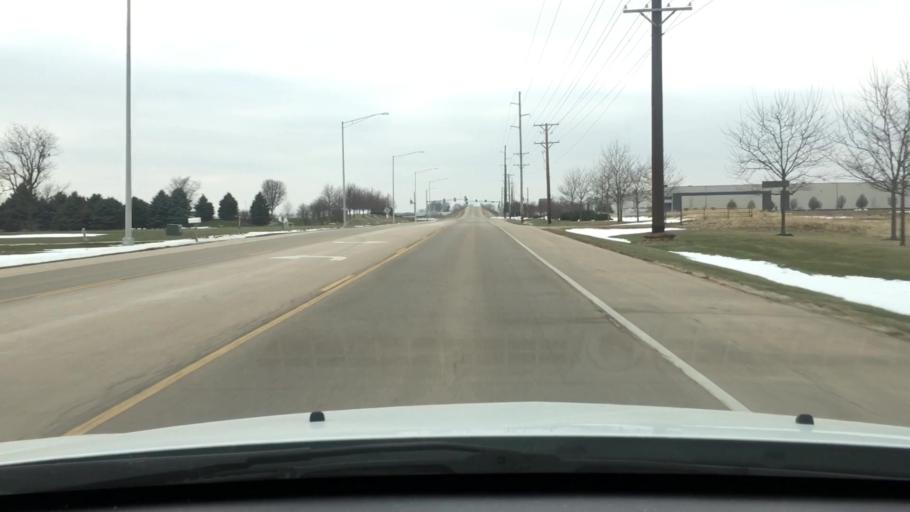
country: US
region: Illinois
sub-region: Ogle County
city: Rochelle
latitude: 41.8981
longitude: -89.0323
